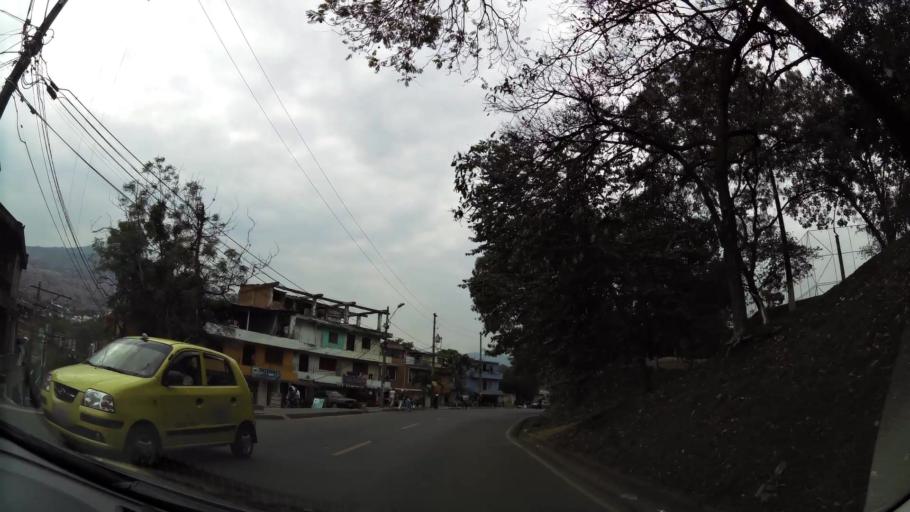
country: CO
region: Antioquia
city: Medellin
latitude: 6.2873
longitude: -75.5645
